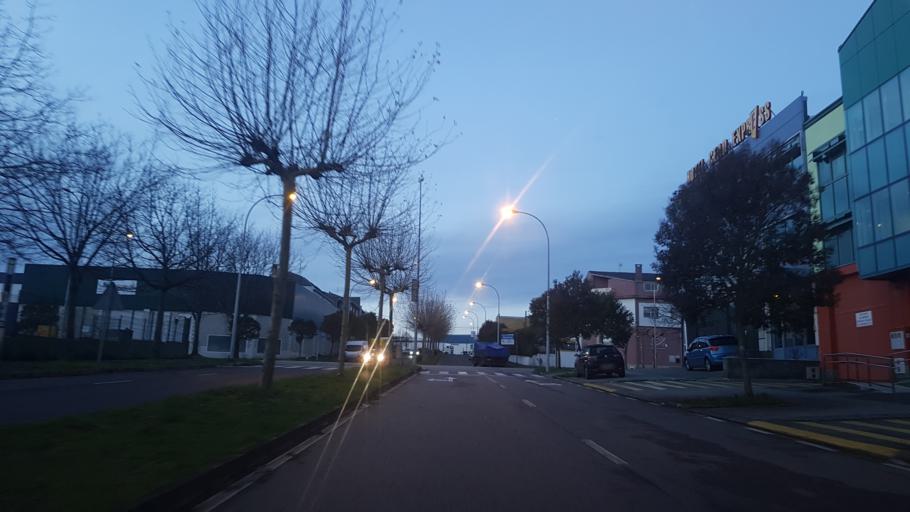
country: ES
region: Galicia
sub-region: Provincia de Lugo
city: Lugo
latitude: 43.0451
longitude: -7.5706
